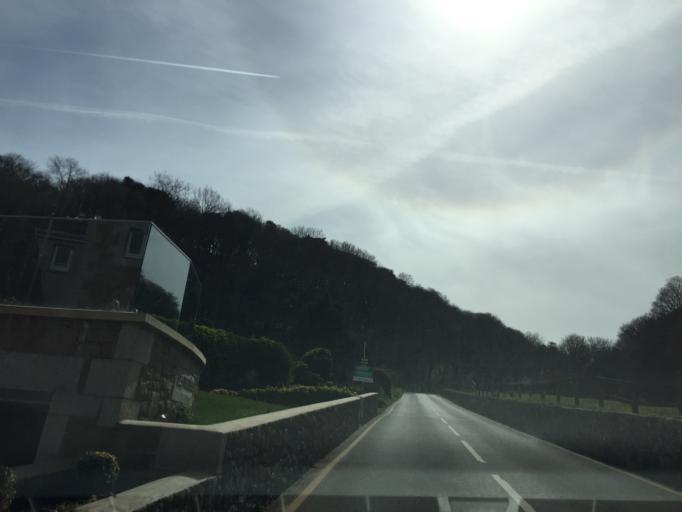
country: JE
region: St Helier
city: Saint Helier
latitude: 49.2456
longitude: -2.2016
